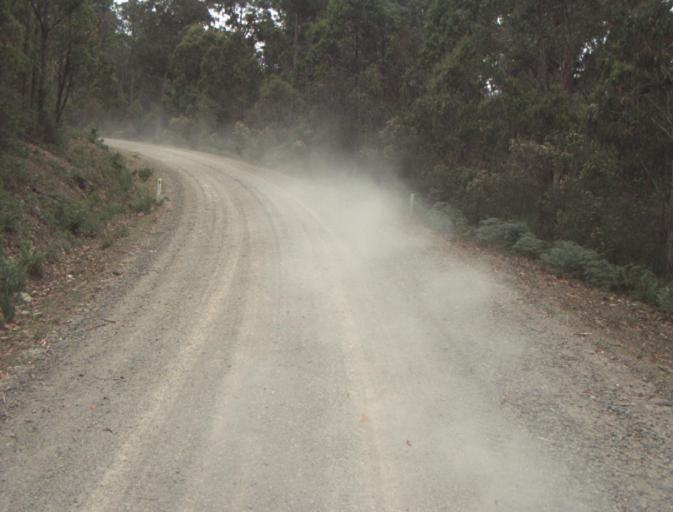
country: AU
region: Tasmania
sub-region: Dorset
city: Scottsdale
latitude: -41.3933
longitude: 147.5127
